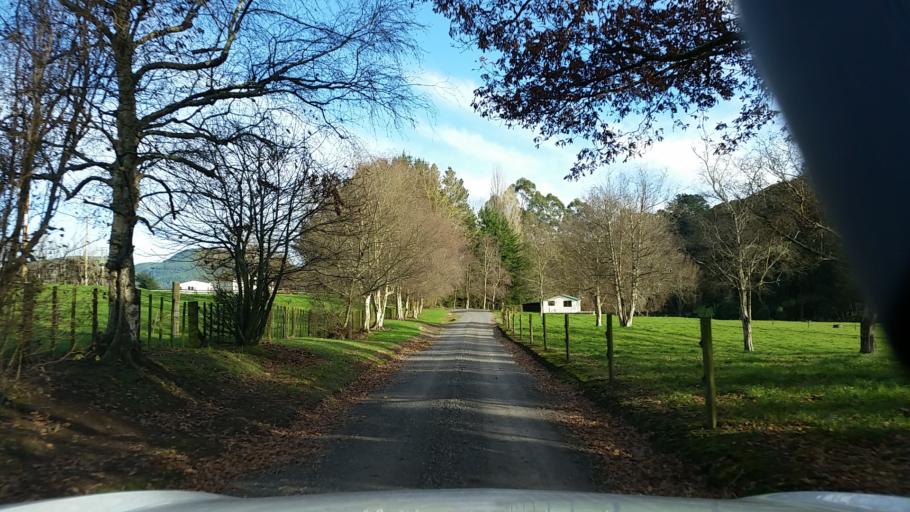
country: NZ
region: Waikato
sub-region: South Waikato District
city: Tokoroa
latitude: -38.3626
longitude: 176.0689
